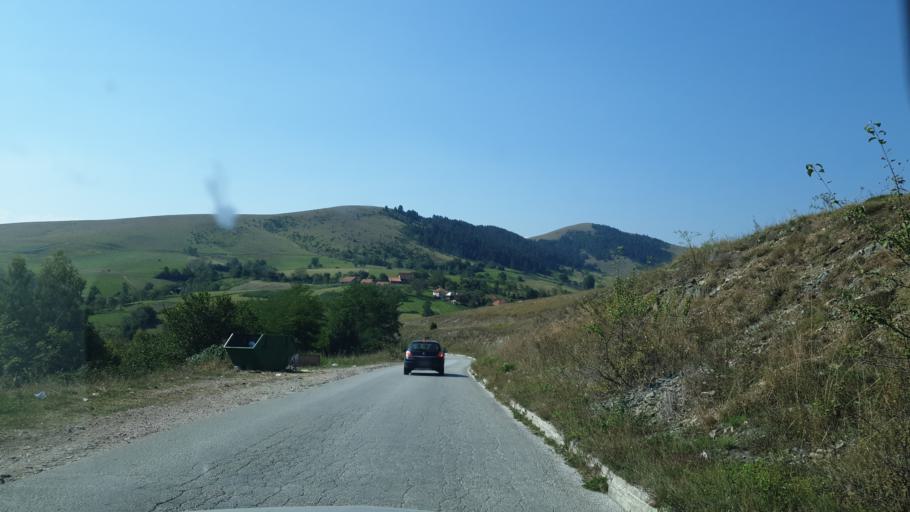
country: RS
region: Central Serbia
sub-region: Zlatiborski Okrug
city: Cajetina
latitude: 43.7193
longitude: 19.7612
